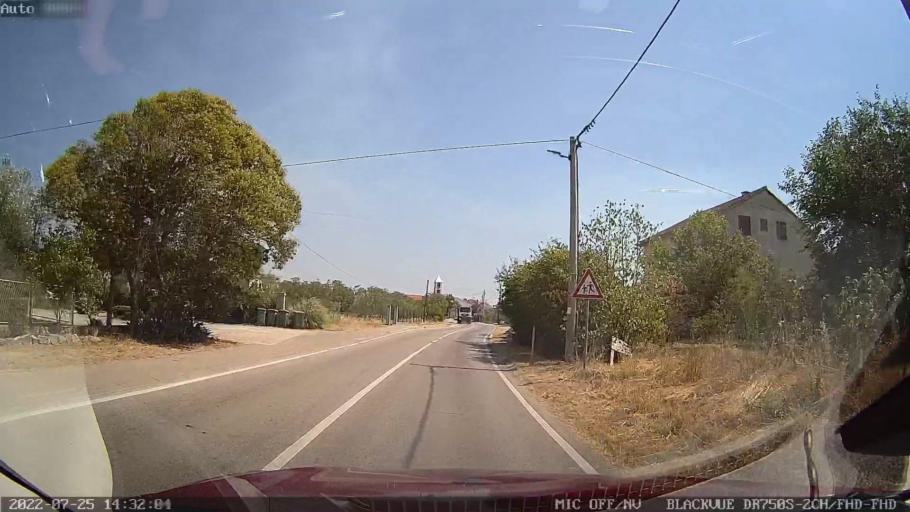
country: HR
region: Zadarska
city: Galovac
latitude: 44.1077
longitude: 15.3773
